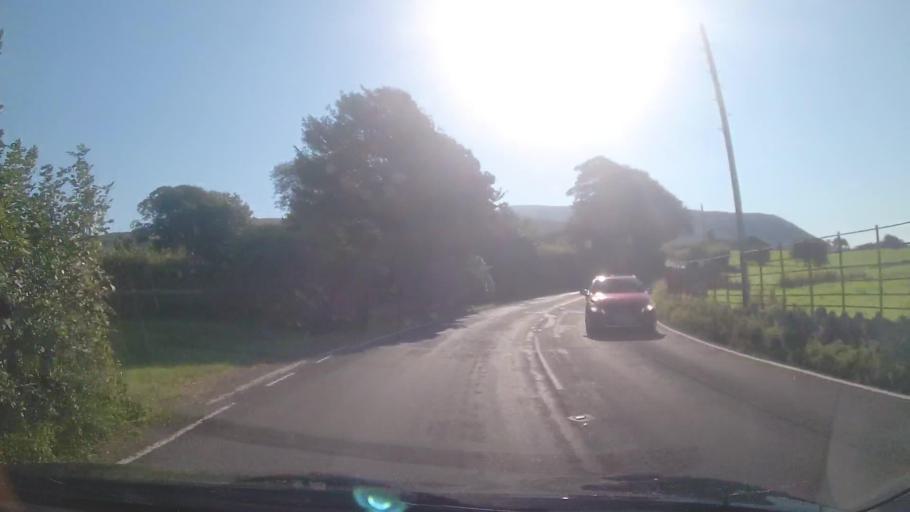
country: GB
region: England
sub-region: Cumbria
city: Millom
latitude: 54.2764
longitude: -3.3680
